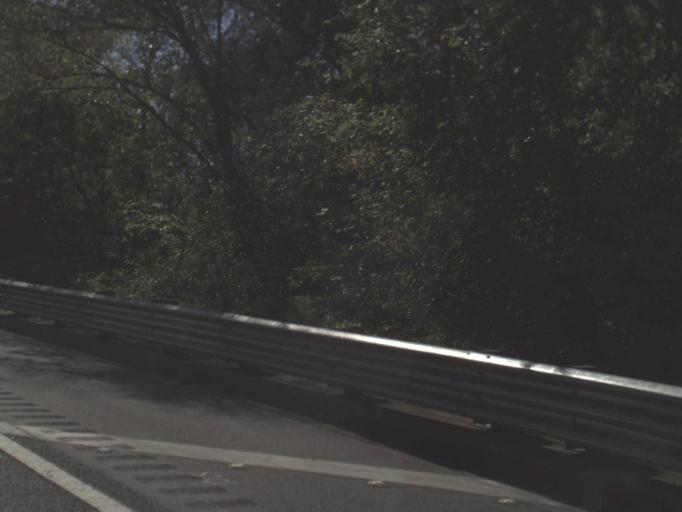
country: US
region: Florida
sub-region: Sumter County
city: Wildwood
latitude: 28.8590
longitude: -82.0913
